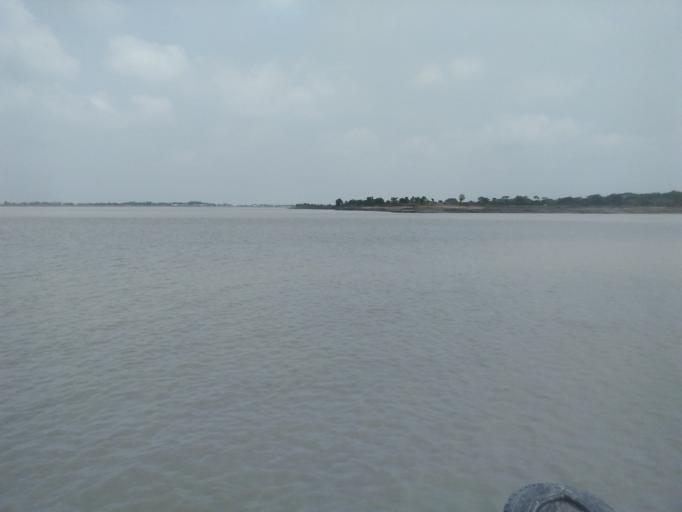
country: BD
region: Khulna
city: Phultala
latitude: 22.6437
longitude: 89.4122
